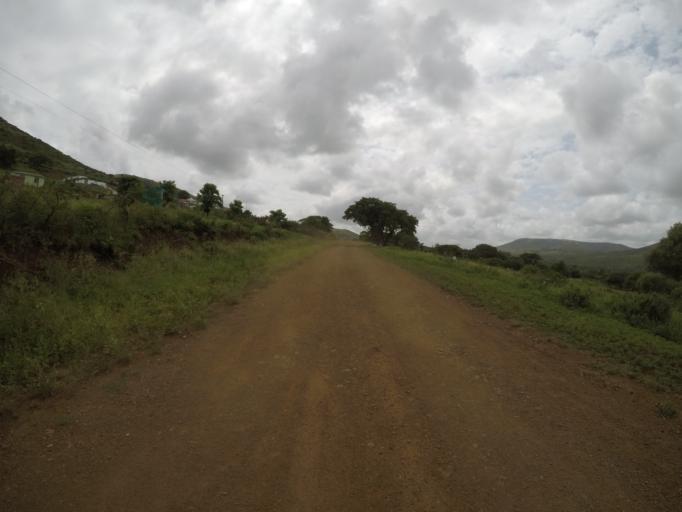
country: ZA
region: KwaZulu-Natal
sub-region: uThungulu District Municipality
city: Empangeni
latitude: -28.5939
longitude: 31.8809
